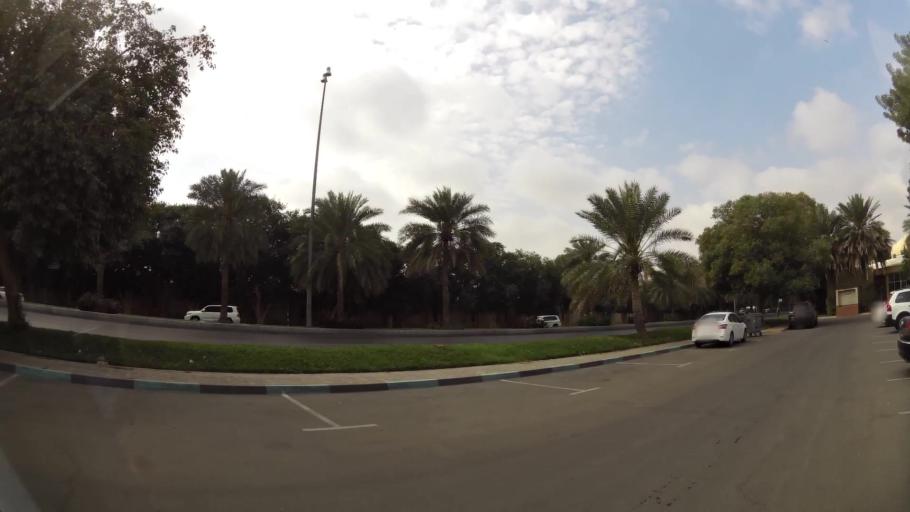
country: AE
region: Abu Dhabi
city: Al Ain
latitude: 24.2249
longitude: 55.7558
